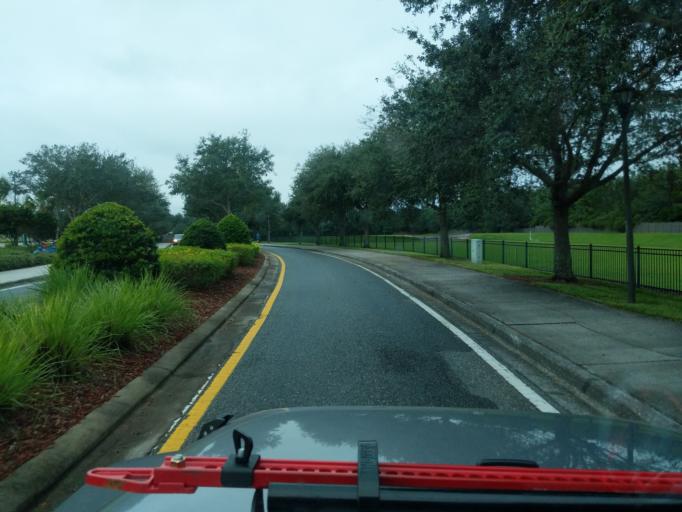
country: US
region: Florida
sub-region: Orange County
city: Winter Garden
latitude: 28.5258
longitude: -81.5888
